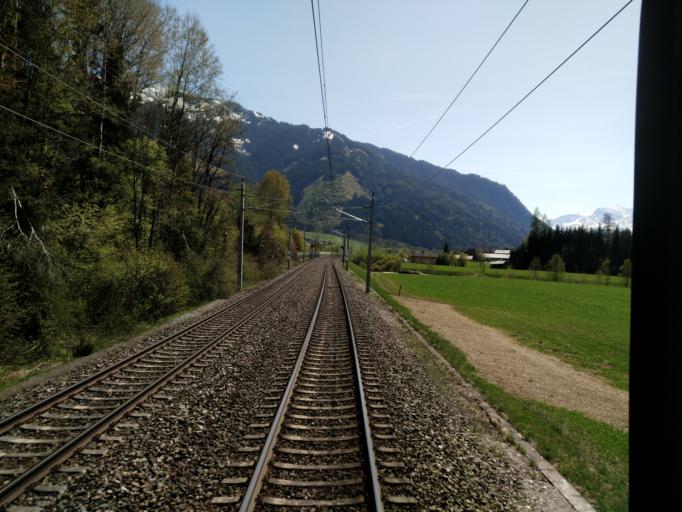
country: AT
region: Salzburg
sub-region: Politischer Bezirk Zell am See
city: Saalfelden am Steinernen Meer
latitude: 47.3987
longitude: 12.8300
